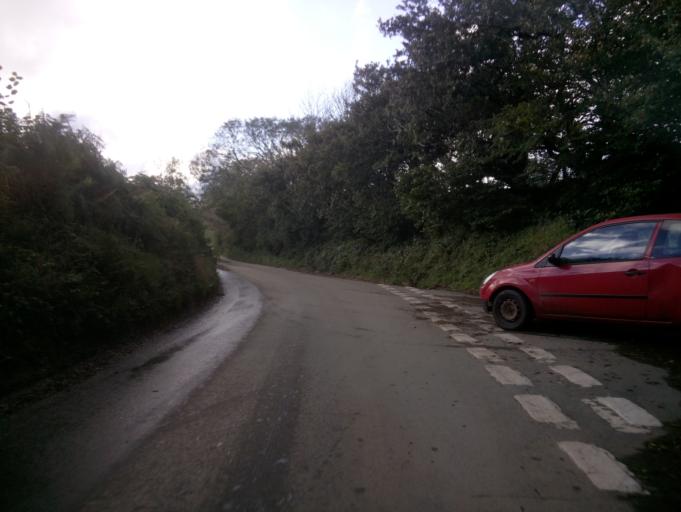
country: GB
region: England
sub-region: Devon
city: Totnes
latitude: 50.3747
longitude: -3.7503
